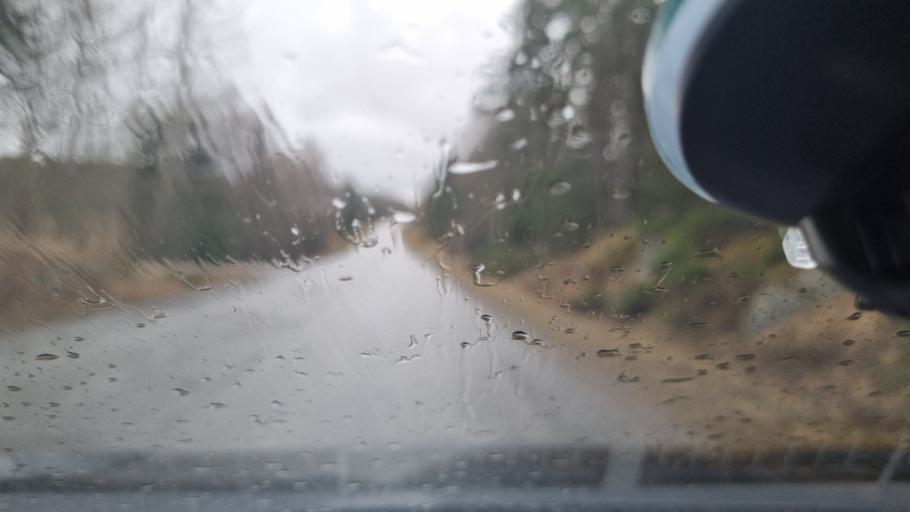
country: SE
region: Stockholm
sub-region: Upplands-Bro Kommun
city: Kungsaengen
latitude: 59.5375
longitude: 17.7434
